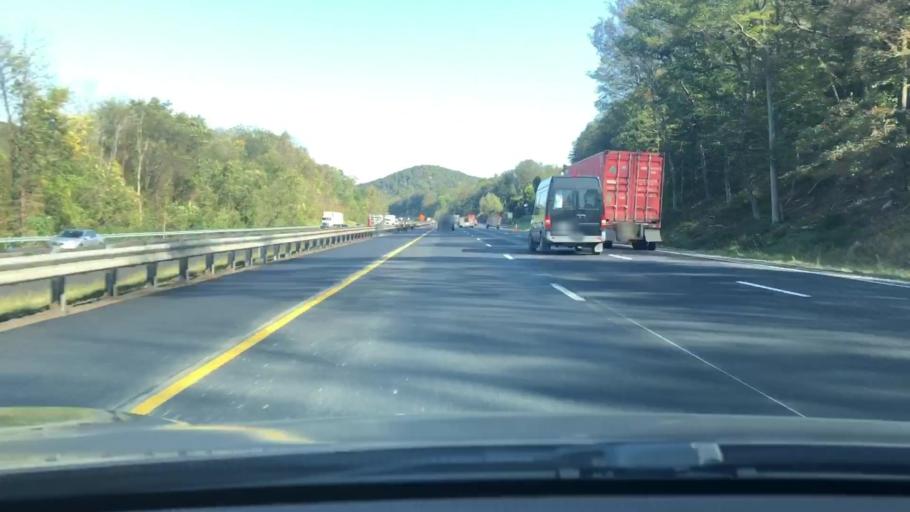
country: US
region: New York
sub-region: Orange County
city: Harriman
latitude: 41.2531
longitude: -74.1638
